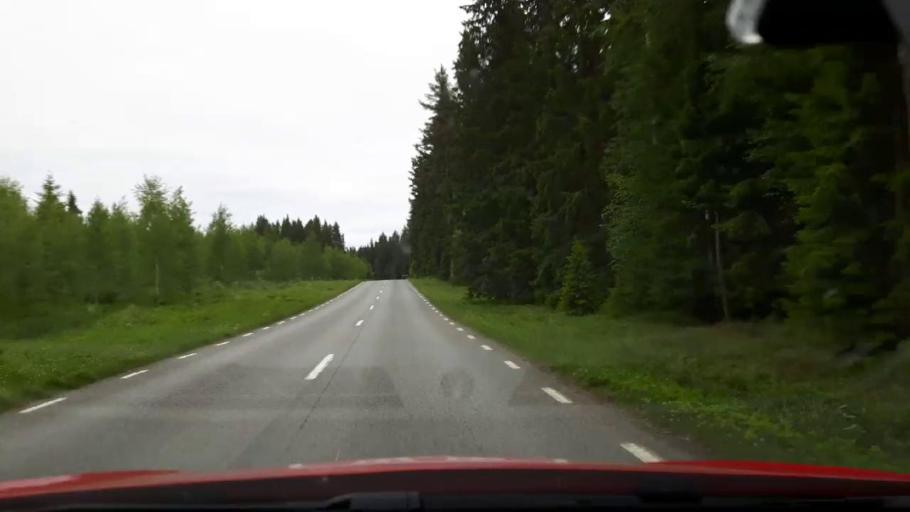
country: SE
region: Jaemtland
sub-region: Stroemsunds Kommun
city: Stroemsund
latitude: 63.4359
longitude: 15.4903
